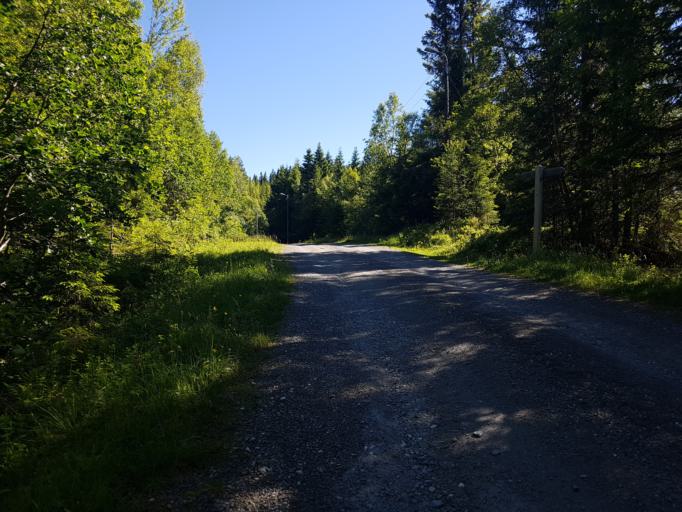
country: NO
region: Sor-Trondelag
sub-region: Trondheim
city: Trondheim
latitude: 63.4344
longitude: 10.2727
